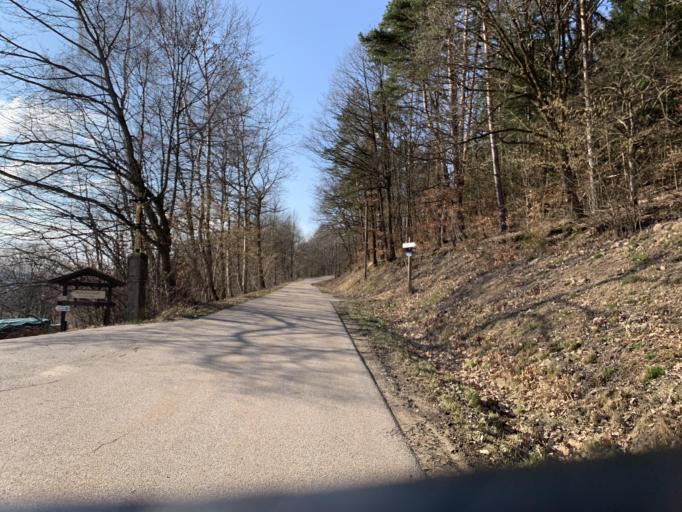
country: DE
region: Bavaria
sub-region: Upper Palatinate
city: Thanstein
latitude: 49.3780
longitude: 12.4423
